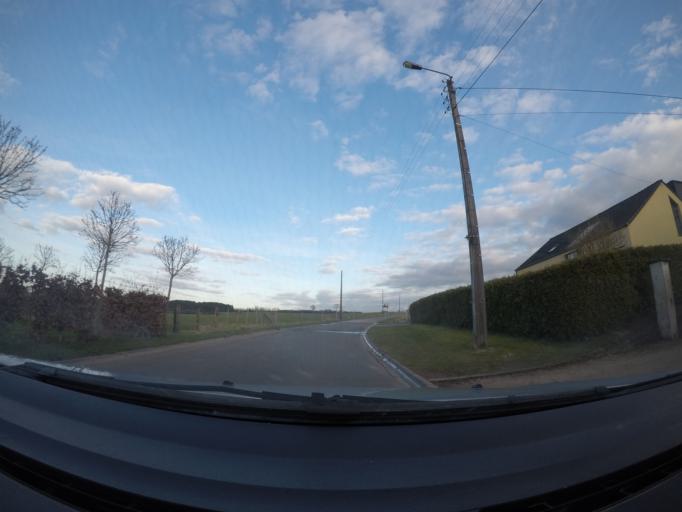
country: BE
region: Wallonia
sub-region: Province du Luxembourg
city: Tintigny
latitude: 49.7058
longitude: 5.5381
